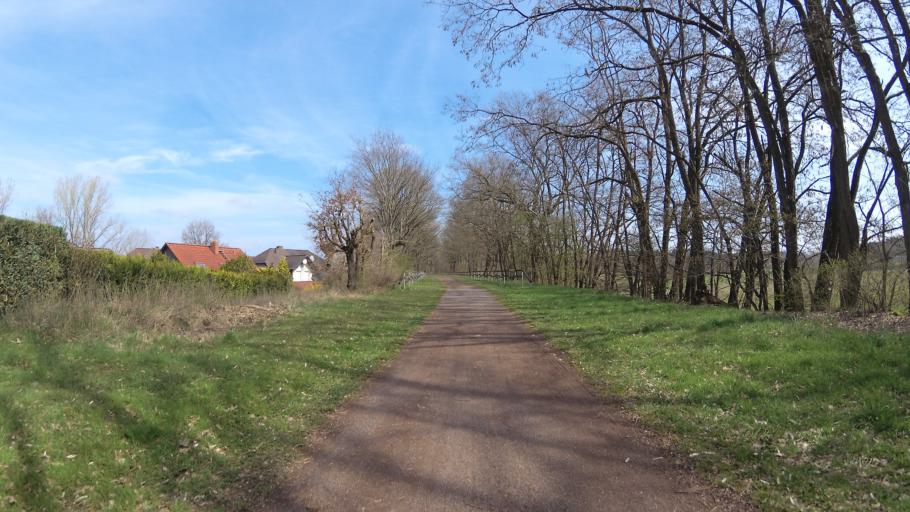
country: DE
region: Rheinland-Pfalz
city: Gries
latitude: 49.4073
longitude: 7.3883
